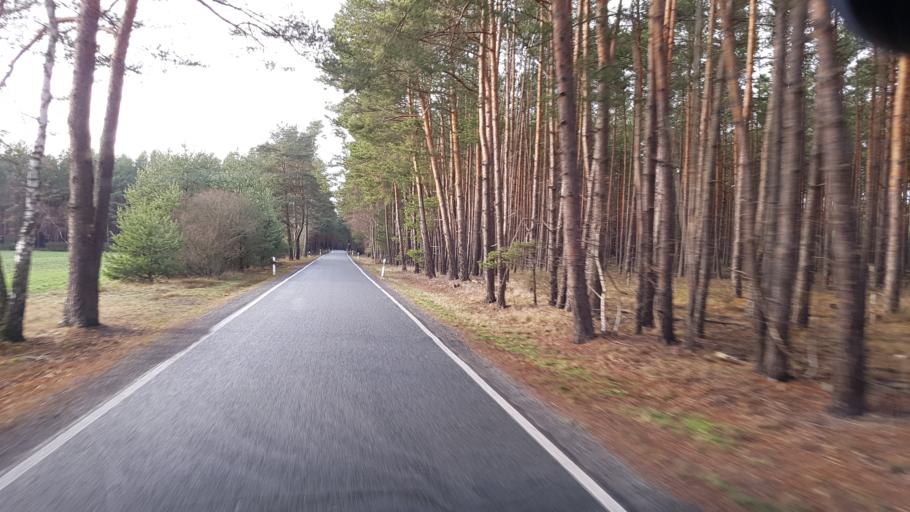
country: DE
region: Brandenburg
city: Bronkow
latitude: 51.6666
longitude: 13.9480
